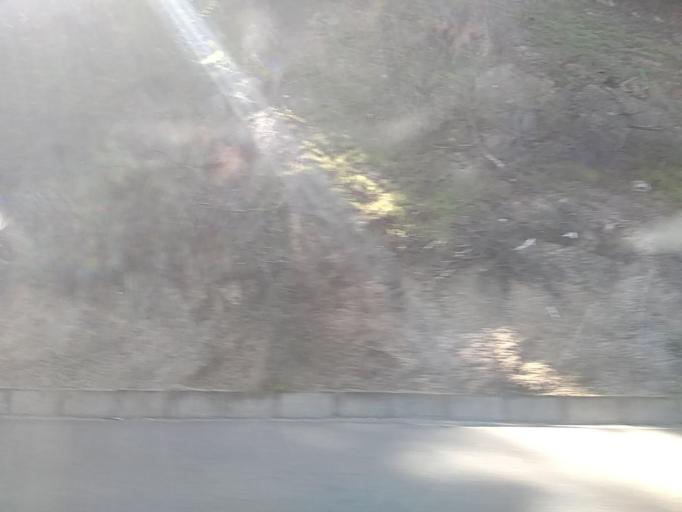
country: CL
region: Valparaiso
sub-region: Provincia de Valparaiso
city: Vina del Mar
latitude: -33.0849
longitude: -71.5452
